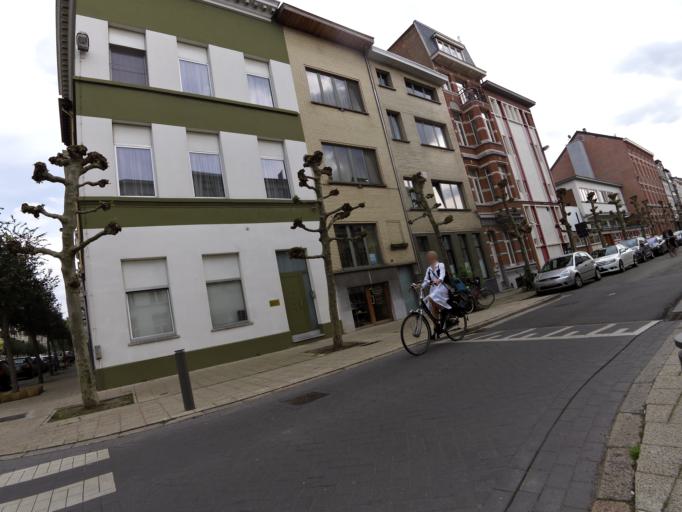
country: BE
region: Flanders
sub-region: Provincie Antwerpen
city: Antwerpen
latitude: 51.2096
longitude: 4.3996
